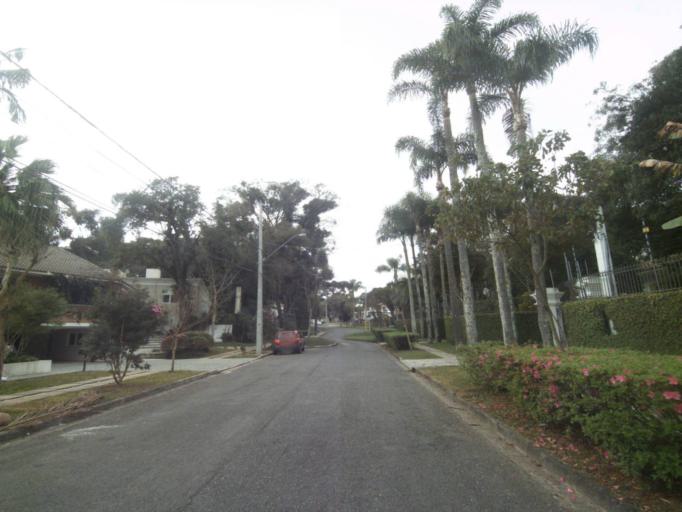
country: BR
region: Parana
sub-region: Curitiba
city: Curitiba
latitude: -25.4463
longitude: -49.3005
